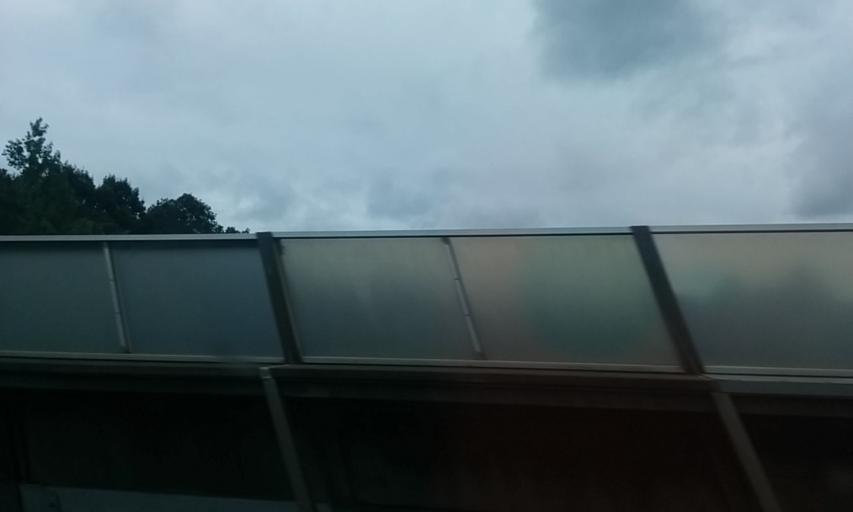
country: JP
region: Tochigi
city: Oyama
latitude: 36.2561
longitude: 139.7691
